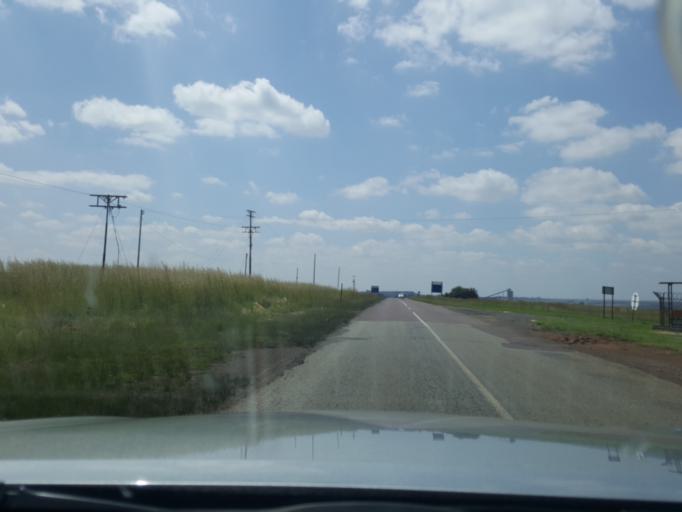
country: ZA
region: Mpumalanga
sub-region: Nkangala District Municipality
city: Middelburg
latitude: -26.0051
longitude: 29.4501
